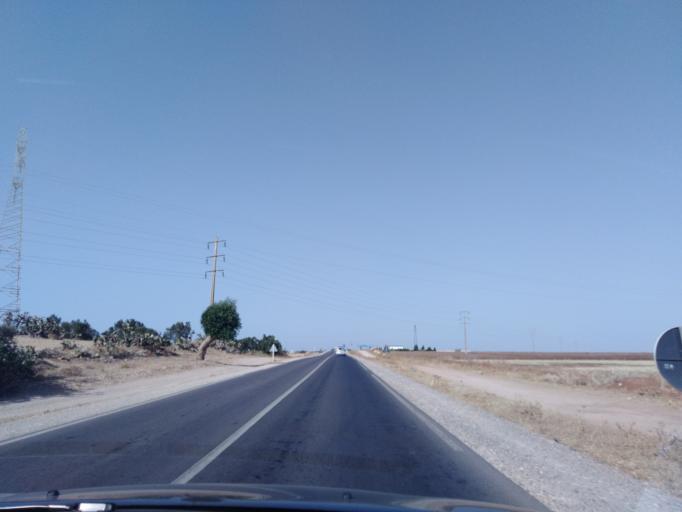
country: MA
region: Doukkala-Abda
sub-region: Safi
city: Safi
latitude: 32.2637
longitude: -8.9545
